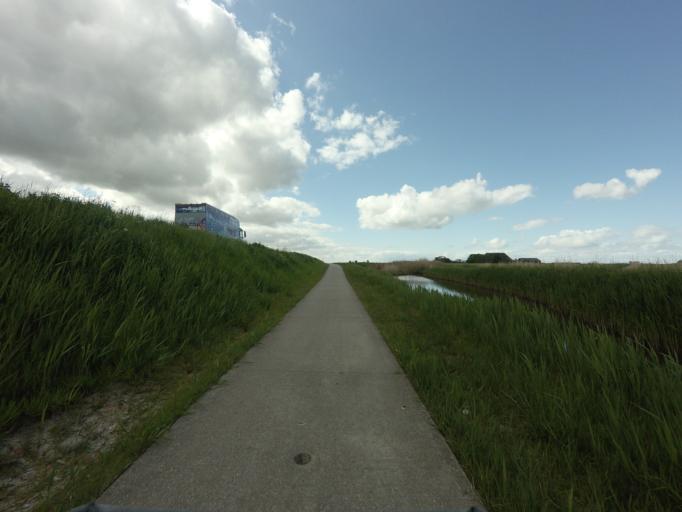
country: NL
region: Friesland
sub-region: Sudwest Fryslan
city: Workum
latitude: 53.0143
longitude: 5.4732
